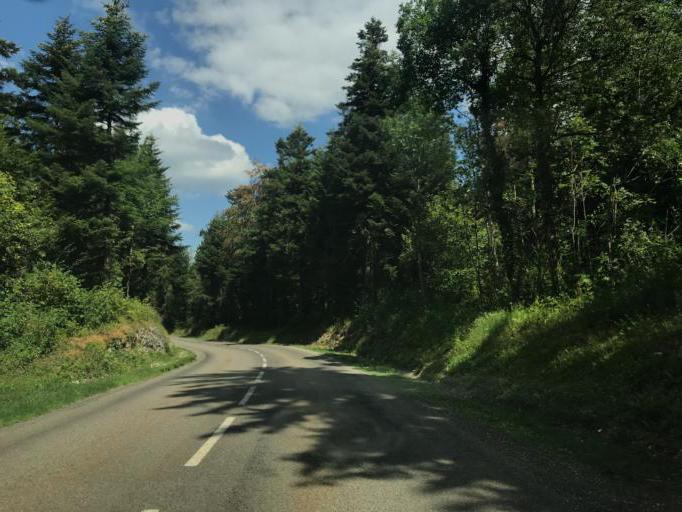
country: FR
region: Franche-Comte
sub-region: Departement du Jura
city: Clairvaux-les-Lacs
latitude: 46.5431
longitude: 5.7943
